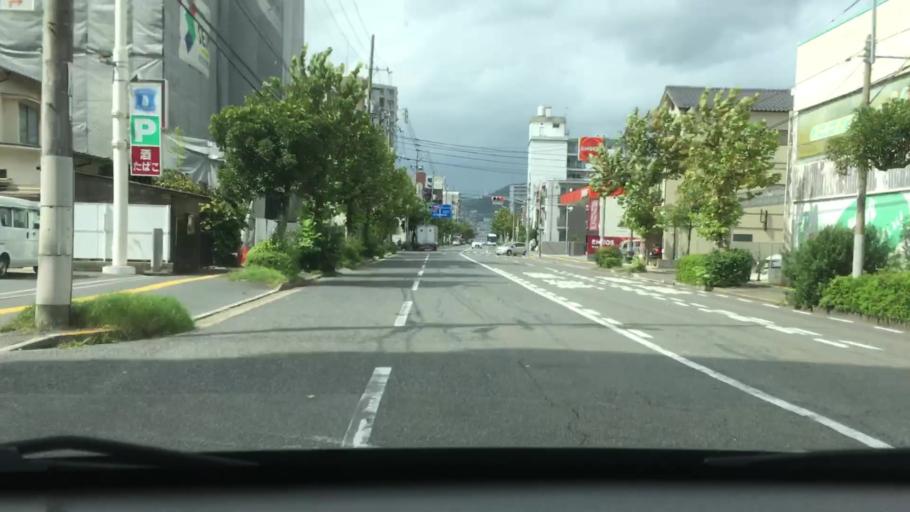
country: JP
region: Hiroshima
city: Hiroshima-shi
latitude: 34.3803
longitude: 132.4432
